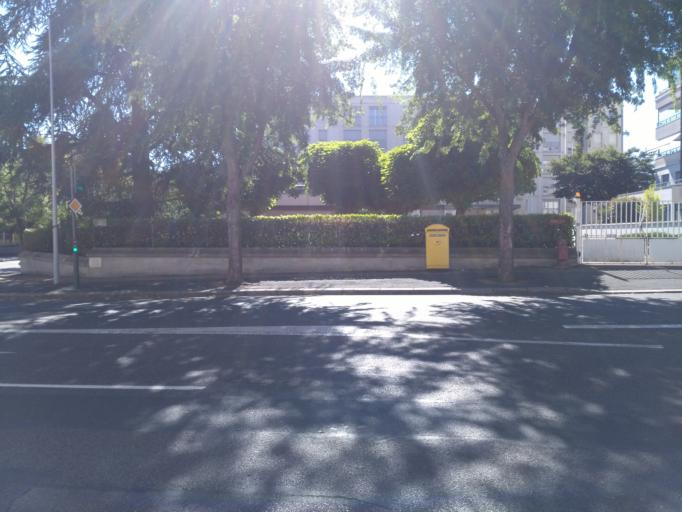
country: FR
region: Rhone-Alpes
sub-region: Departement du Rhone
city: Villefranche-sur-Saone
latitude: 45.9916
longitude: 4.7152
